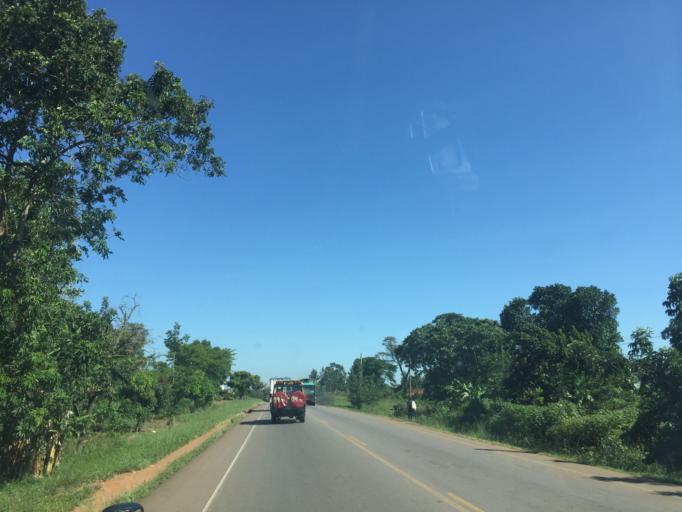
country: UG
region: Central Region
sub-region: Luwero District
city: Wobulenzi
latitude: 0.7706
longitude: 32.5122
